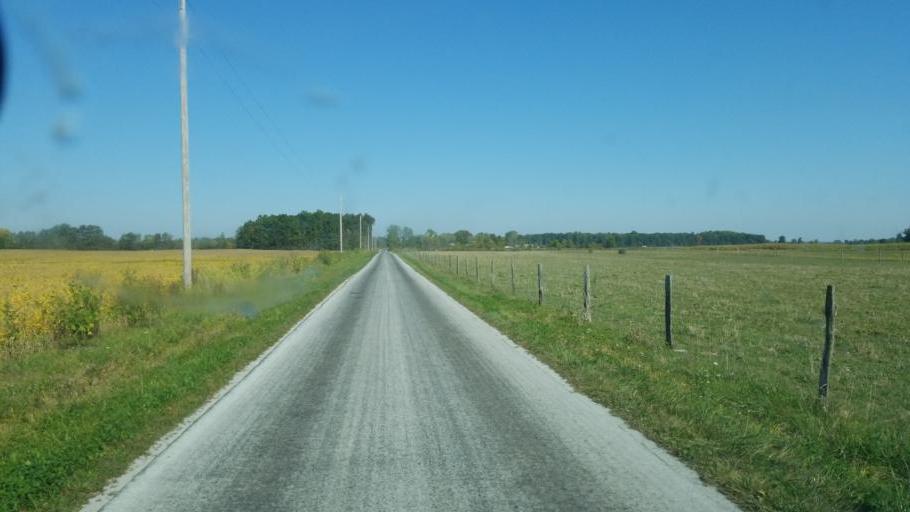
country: US
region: Ohio
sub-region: Hardin County
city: Kenton
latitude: 40.5694
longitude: -83.4878
